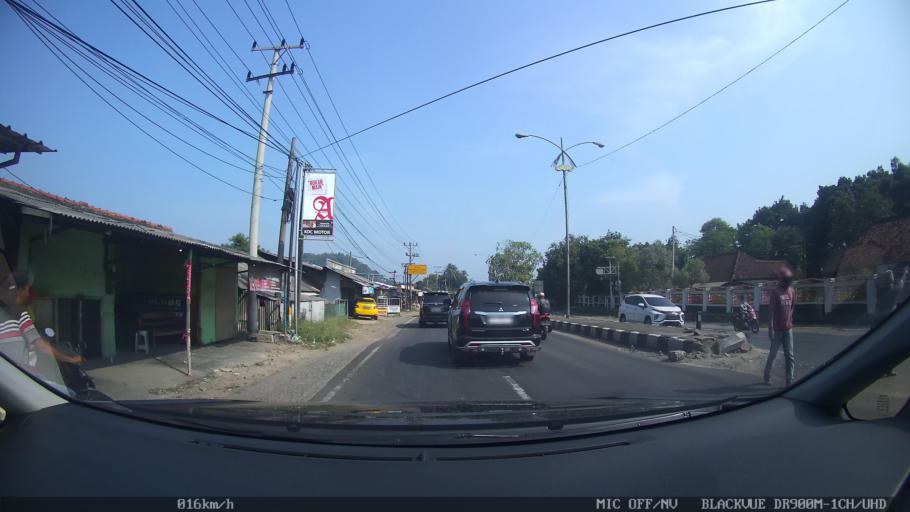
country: ID
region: Lampung
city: Natar
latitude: -5.2407
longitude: 105.1736
